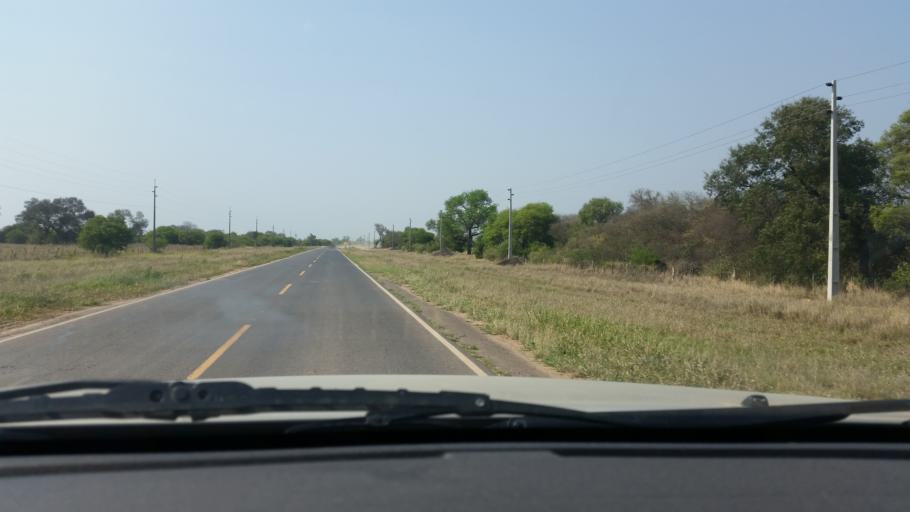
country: PY
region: Boqueron
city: Filadelfia
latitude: -22.4233
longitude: -60.0278
